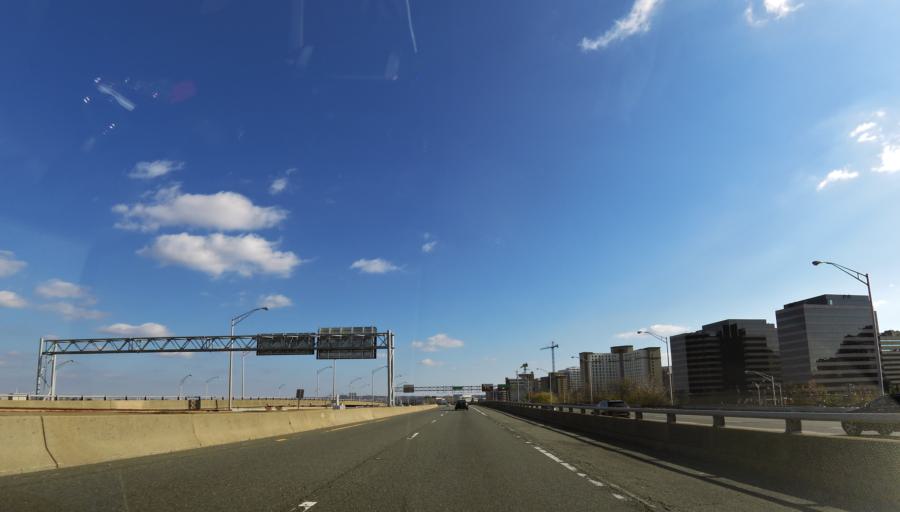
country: US
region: Washington, D.C.
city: Washington, D.C.
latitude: 38.8671
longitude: -77.0600
